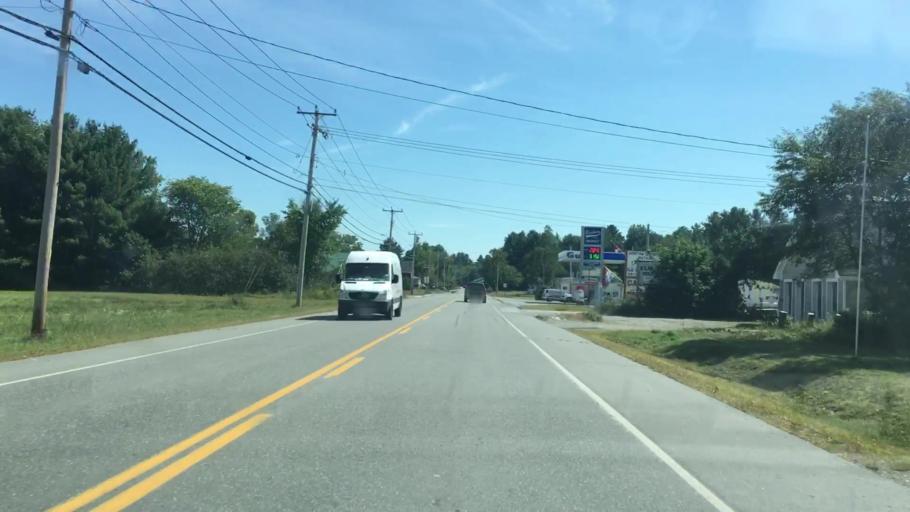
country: US
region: Maine
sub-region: Piscataquis County
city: Milo
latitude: 45.2461
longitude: -68.9769
